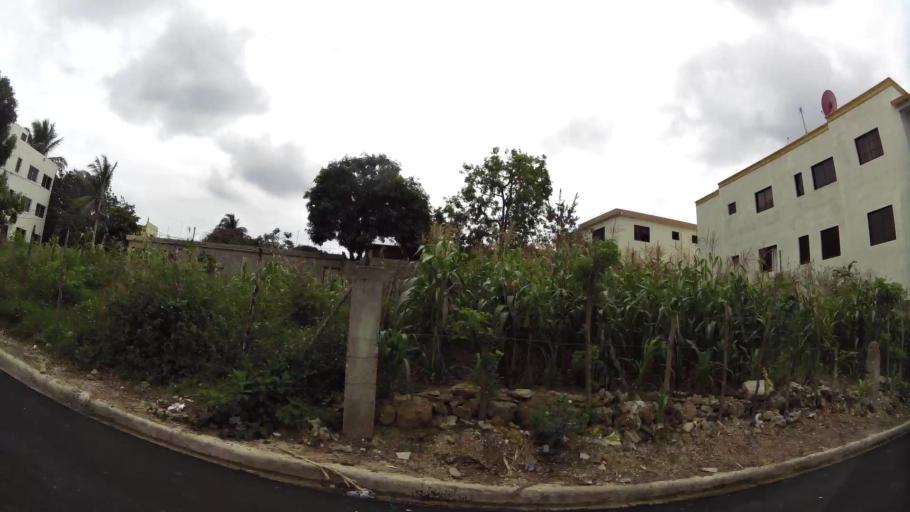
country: DO
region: Santiago
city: Santiago de los Caballeros
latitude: 19.4363
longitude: -70.6711
